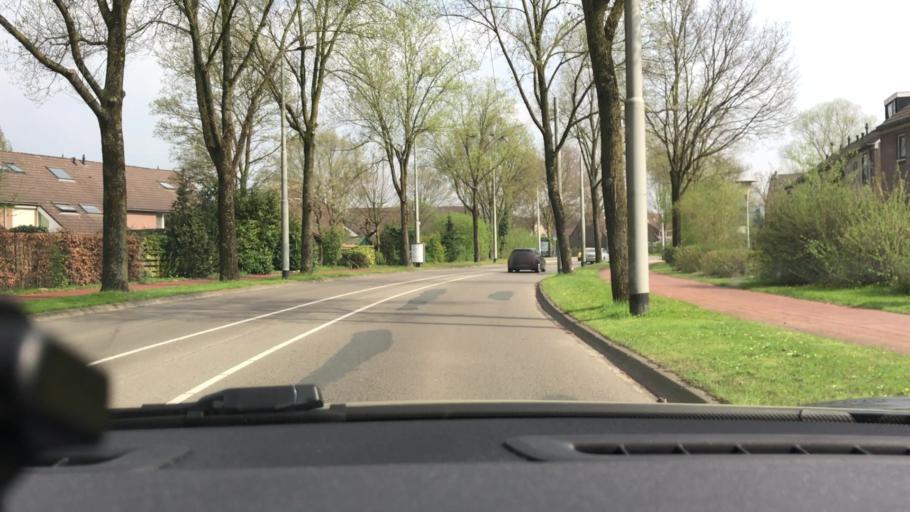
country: NL
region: Gelderland
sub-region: Gemeente Renkum
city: Oosterbeek
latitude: 51.9629
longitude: 5.8682
